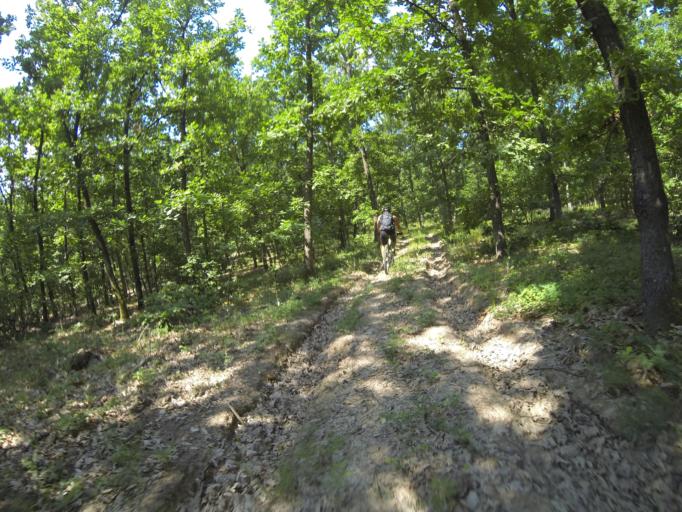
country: RO
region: Gorj
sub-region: Comuna Crusetu
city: Crusetu
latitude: 44.6147
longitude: 23.6373
